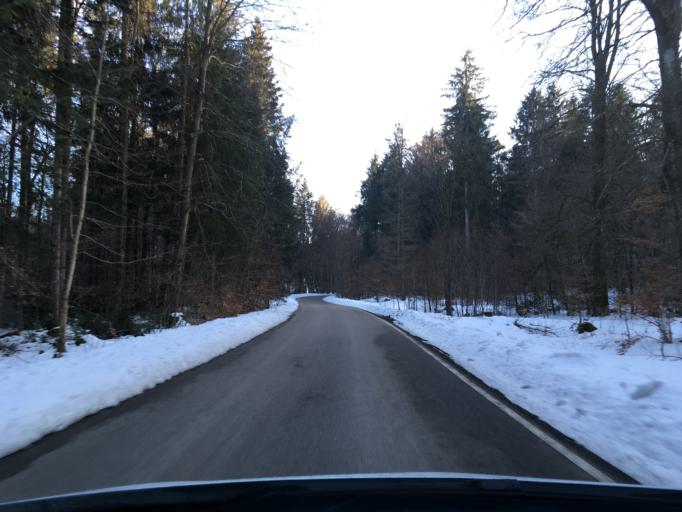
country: DE
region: Bavaria
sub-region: Upper Bavaria
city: Albaching
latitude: 48.1131
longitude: 12.0812
